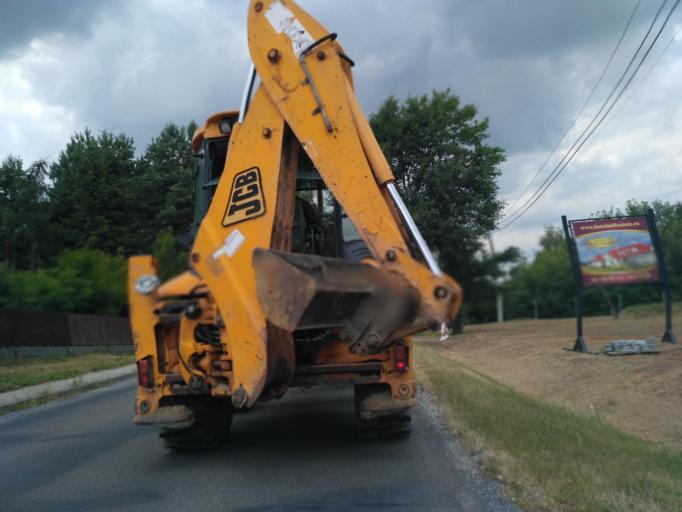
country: PL
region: Subcarpathian Voivodeship
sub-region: Powiat debicki
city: Zyrakow
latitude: 50.0491
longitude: 21.3415
